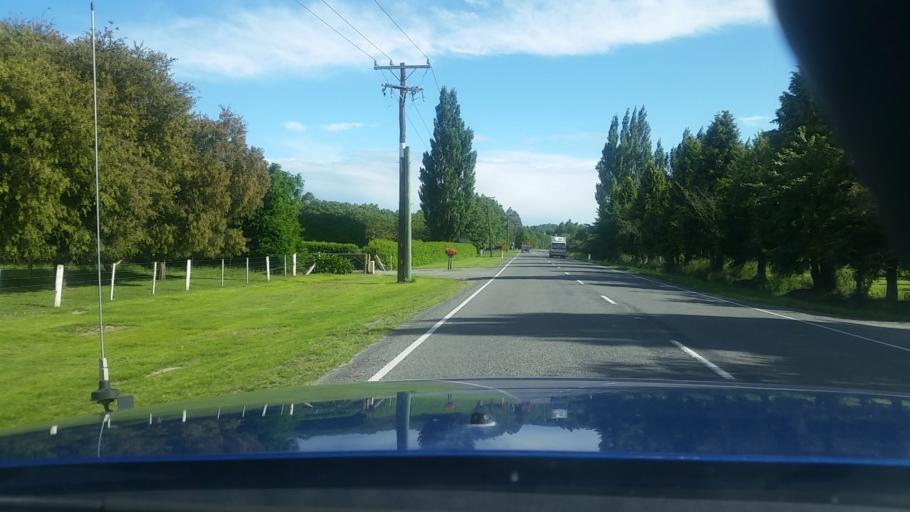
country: NZ
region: Canterbury
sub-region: Ashburton District
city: Ashburton
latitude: -43.8706
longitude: 171.7274
